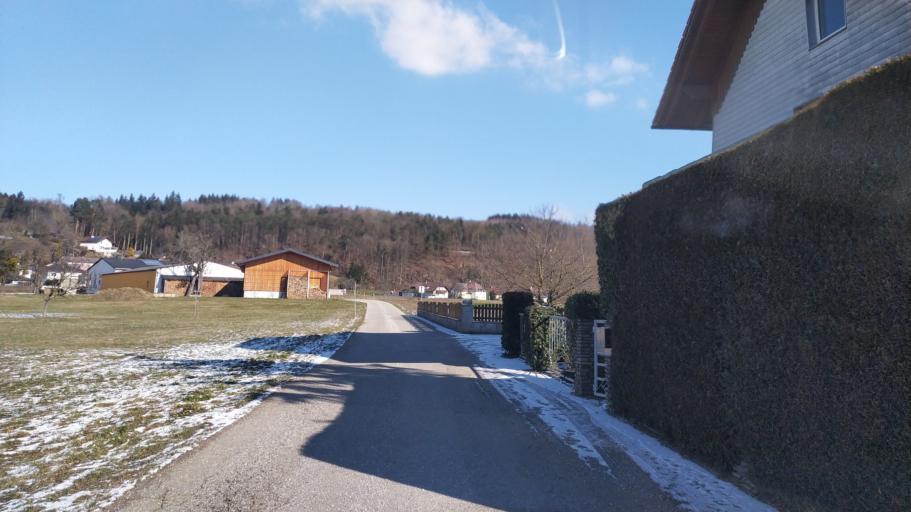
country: AT
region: Upper Austria
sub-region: Politischer Bezirk Urfahr-Umgebung
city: Feldkirchen an der Donau
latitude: 48.3601
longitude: 14.0334
